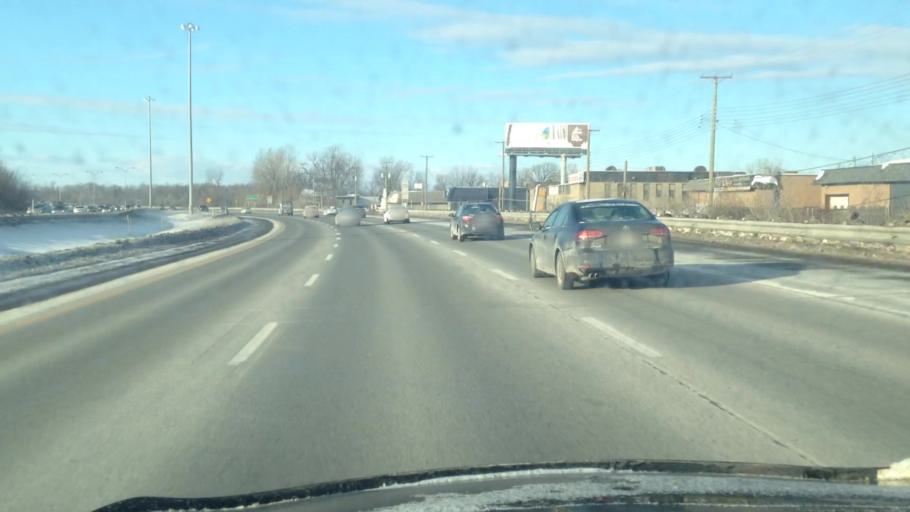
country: CA
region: Quebec
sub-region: Laurentides
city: Boisbriand
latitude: 45.6037
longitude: -73.8054
